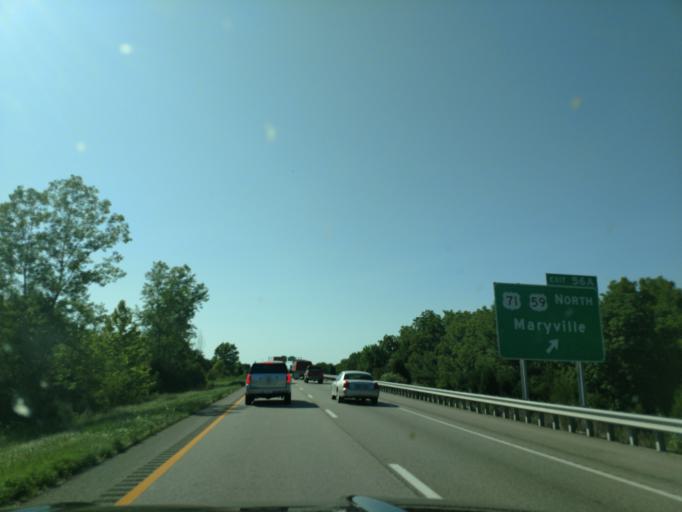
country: US
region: Missouri
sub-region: Andrew County
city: Country Club Village
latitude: 39.8834
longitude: -94.8516
